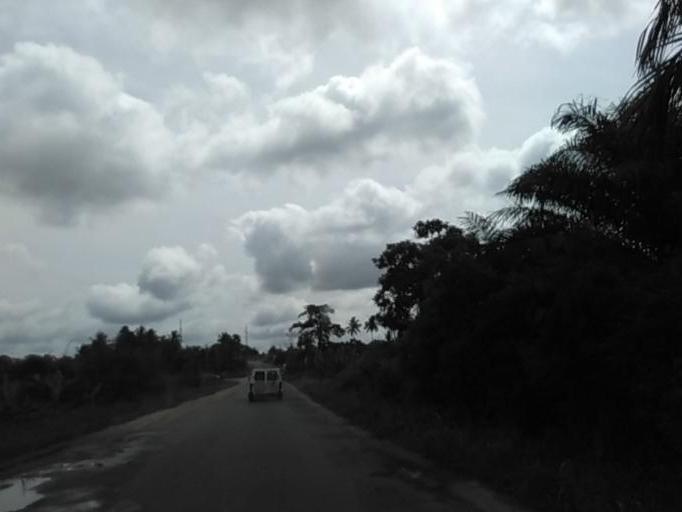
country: GH
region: Ashanti
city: Mamponteng
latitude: 6.7454
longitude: -1.4576
